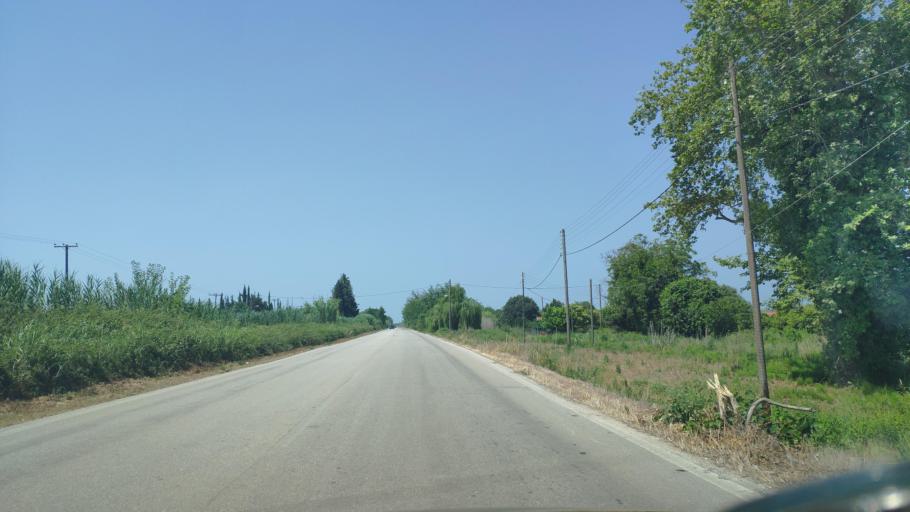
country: GR
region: Epirus
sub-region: Nomos Artas
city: Aneza
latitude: 39.1113
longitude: 20.9245
